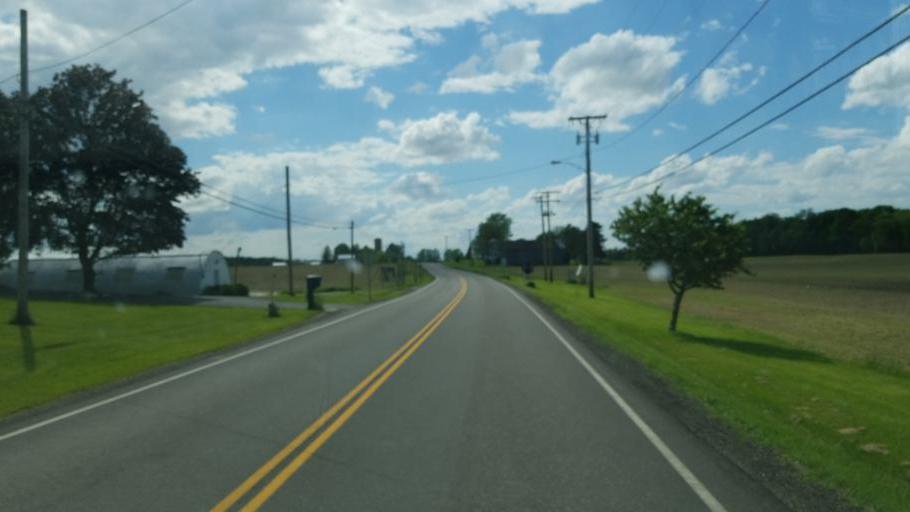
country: US
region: Ohio
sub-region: Huron County
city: Plymouth
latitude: 40.9694
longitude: -82.6100
